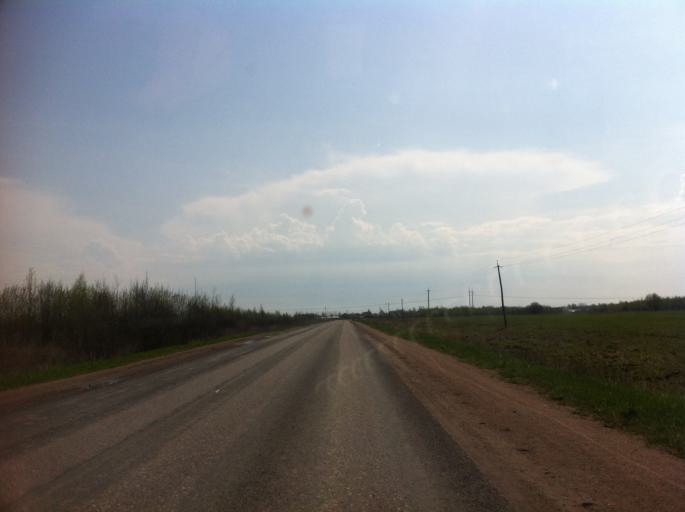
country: RU
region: Pskov
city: Pskov
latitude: 57.8034
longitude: 28.1856
